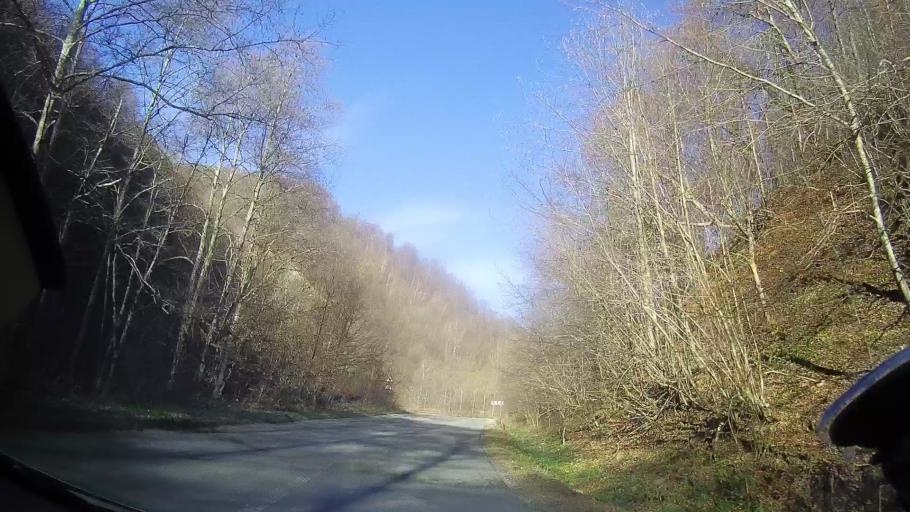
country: RO
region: Cluj
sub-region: Comuna Sacueu
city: Sacuieu
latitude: 46.8424
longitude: 22.8611
